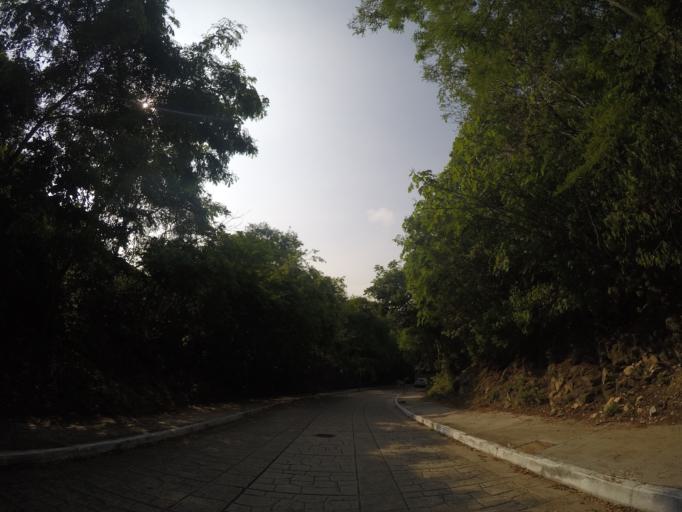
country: MX
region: Oaxaca
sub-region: Santa Maria Huatulco
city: Crucecita
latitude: 15.7563
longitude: -96.1283
